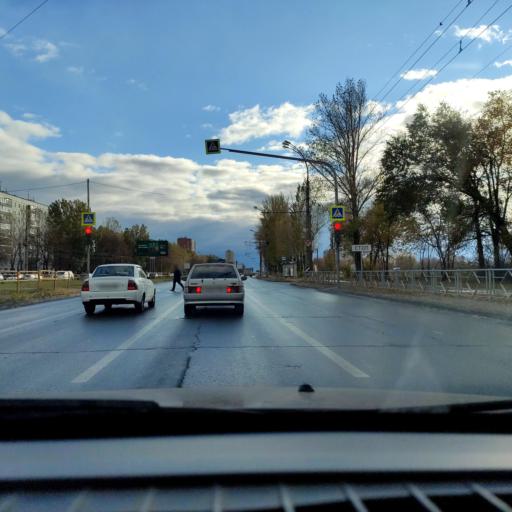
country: RU
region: Samara
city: Tol'yatti
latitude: 53.5193
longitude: 49.2584
